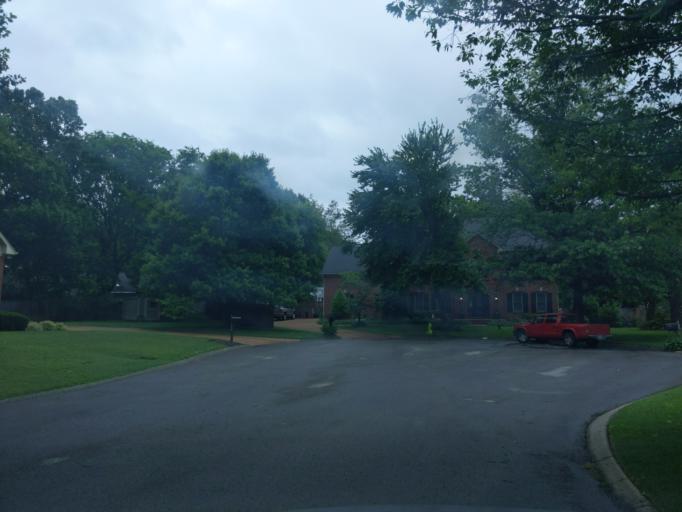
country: US
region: Tennessee
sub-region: Williamson County
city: Brentwood
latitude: 36.0440
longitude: -86.7518
